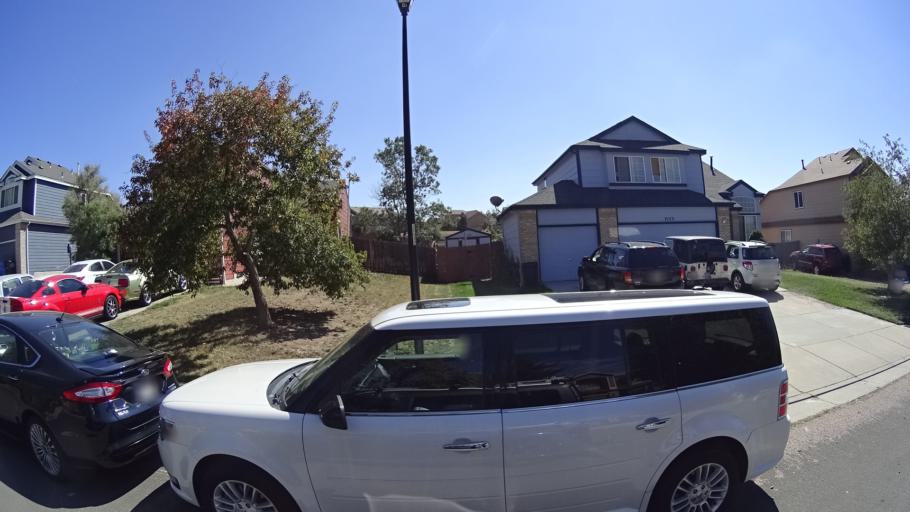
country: US
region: Colorado
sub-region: El Paso County
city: Cimarron Hills
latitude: 38.8983
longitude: -104.6978
